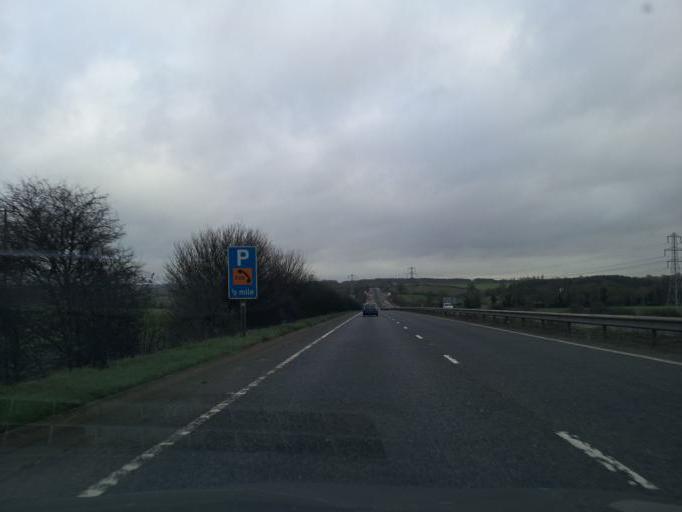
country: GB
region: England
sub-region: Norfolk
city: Norwich
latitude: 52.5940
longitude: 1.2904
